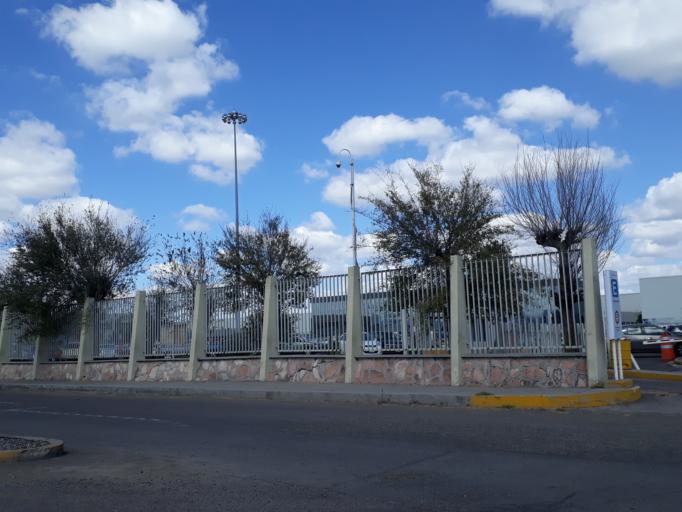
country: MX
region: Aguascalientes
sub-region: Aguascalientes
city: San Sebastian [Fraccionamiento]
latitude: 21.8035
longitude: -102.2836
